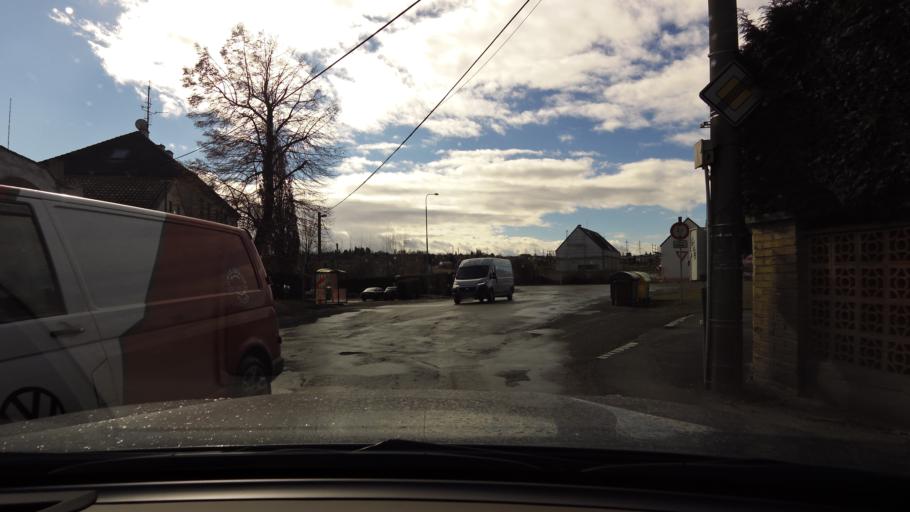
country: CZ
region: Plzensky
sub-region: Okres Plzen-Mesto
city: Pilsen
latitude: 49.7755
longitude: 13.3889
